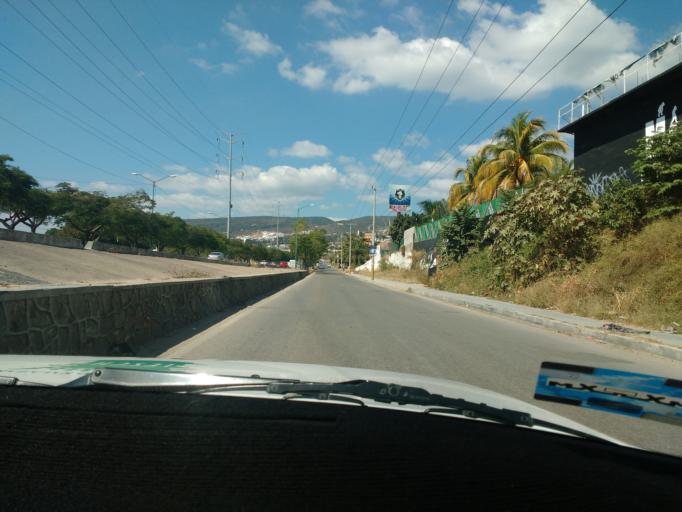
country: MX
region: Chiapas
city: Tuxtla Gutierrez
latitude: 16.7717
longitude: -93.1150
